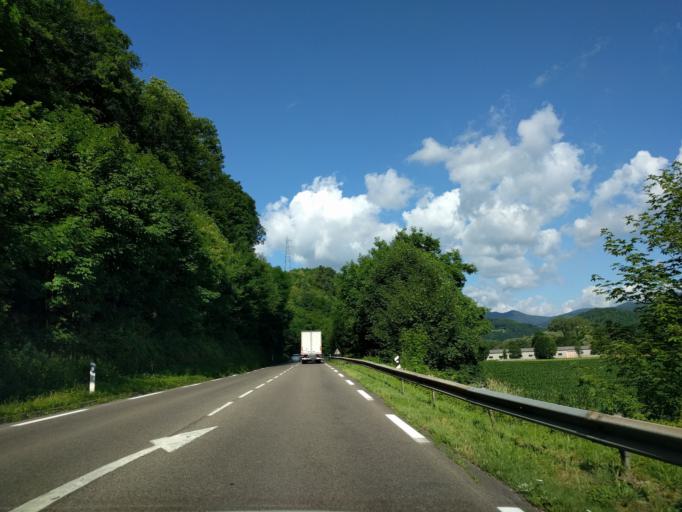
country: FR
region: Alsace
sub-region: Departement du Haut-Rhin
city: Liepvre
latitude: 48.2664
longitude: 7.3028
